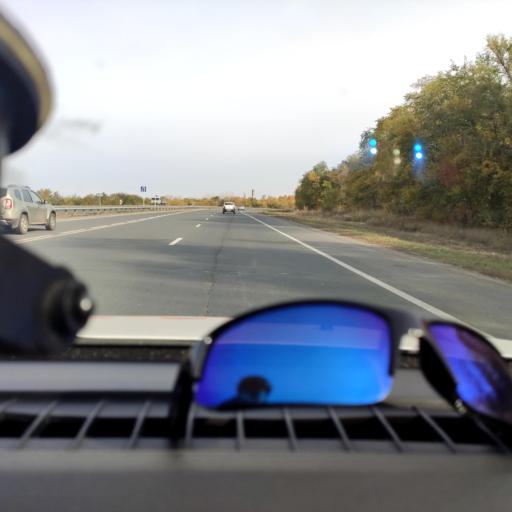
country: RU
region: Samara
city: Novokuybyshevsk
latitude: 53.0484
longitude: 50.0084
